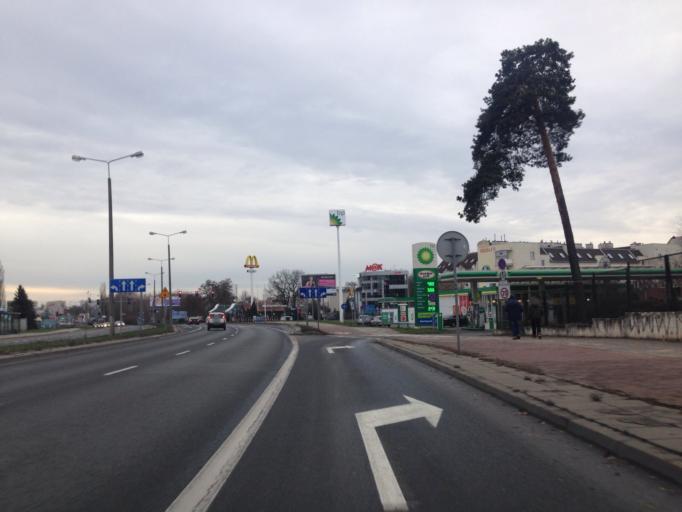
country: PL
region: Kujawsko-Pomorskie
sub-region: Torun
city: Torun
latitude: 53.0328
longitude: 18.6110
